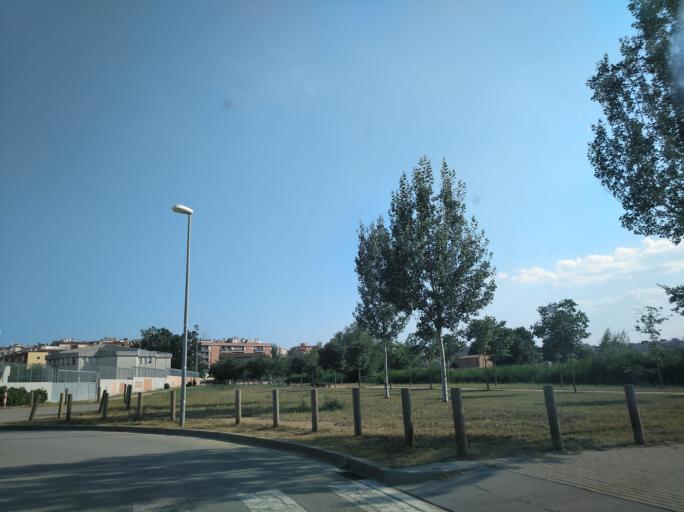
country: ES
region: Catalonia
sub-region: Provincia de Girona
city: Girona
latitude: 41.9813
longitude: 2.8092
